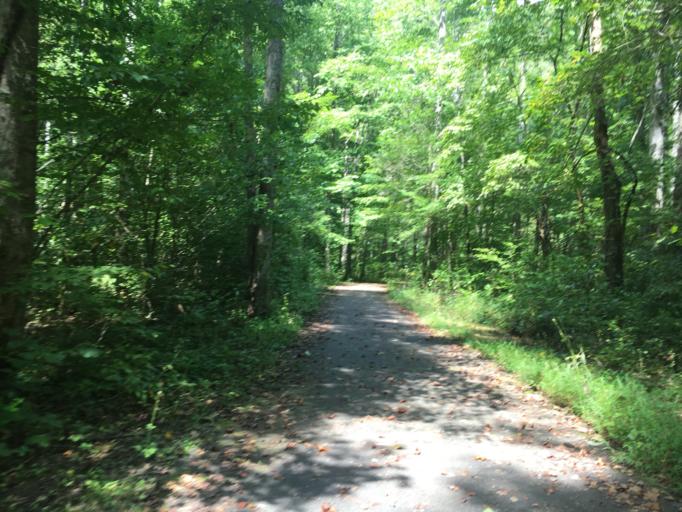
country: US
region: North Carolina
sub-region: Graham County
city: Robbinsville
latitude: 35.2764
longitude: -83.6802
